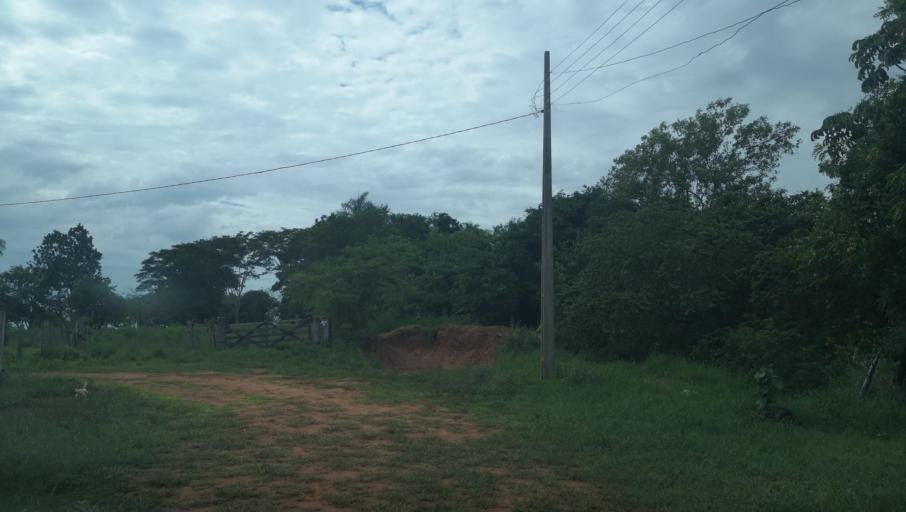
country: PY
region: San Pedro
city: Capiibary
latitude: -24.7172
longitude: -56.0127
